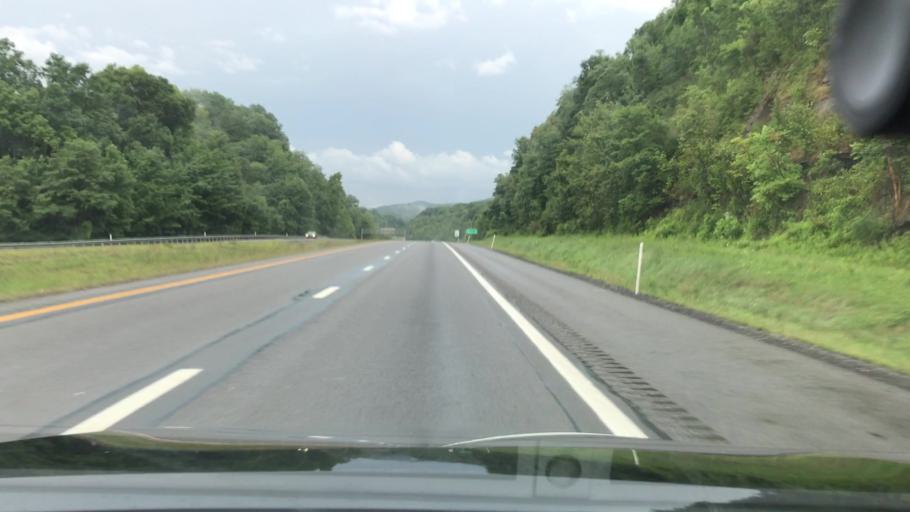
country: US
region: West Virginia
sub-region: Fayette County
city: Oak Hill
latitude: 37.9674
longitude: -81.2745
